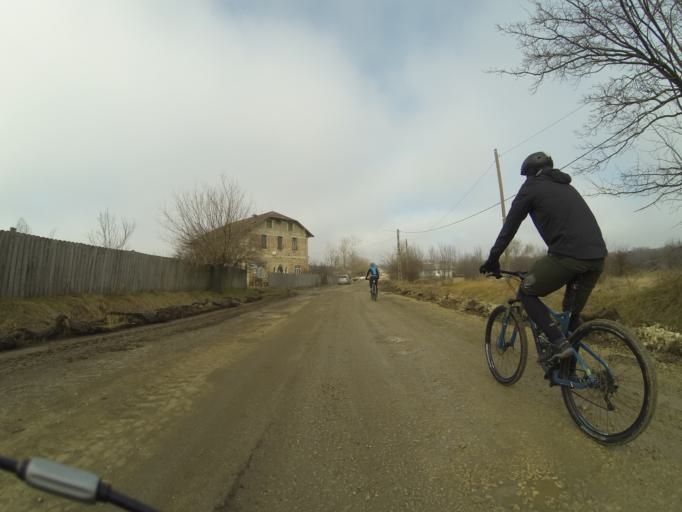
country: RO
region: Mehedinti
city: Dumbrava de Sus
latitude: 44.4925
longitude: 23.0931
